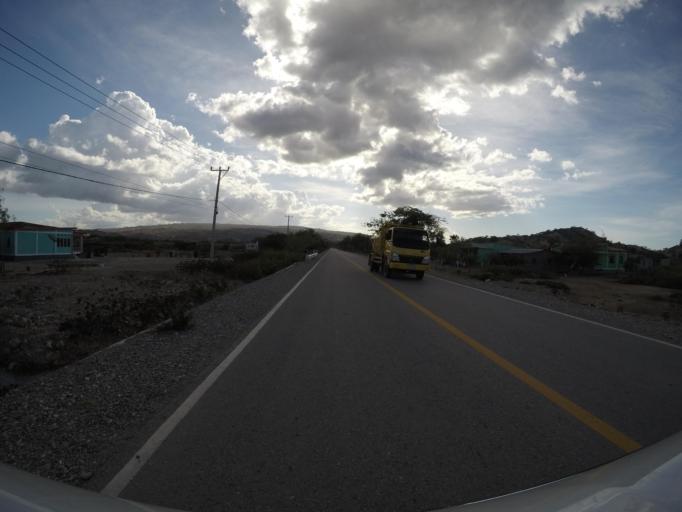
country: TL
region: Baucau
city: Baucau
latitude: -8.4744
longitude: 126.5183
